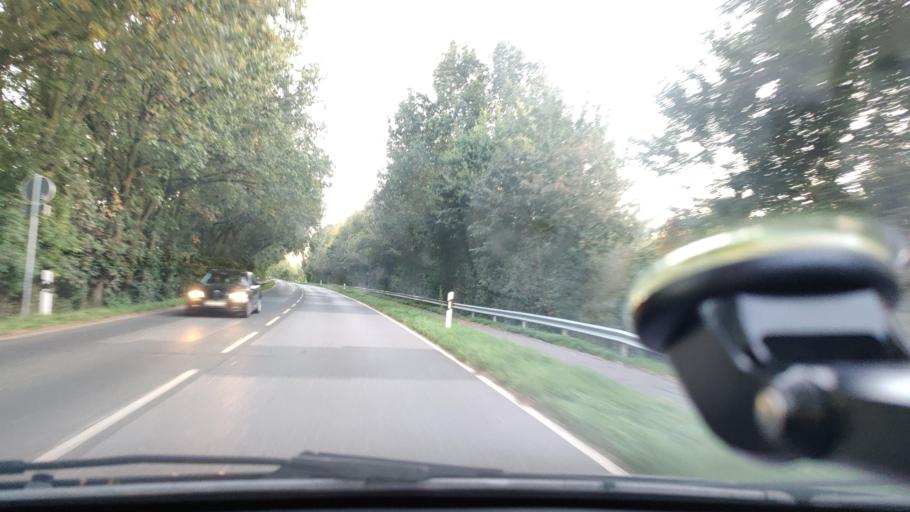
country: DE
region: North Rhine-Westphalia
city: Kalkar
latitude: 51.7372
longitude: 6.3017
